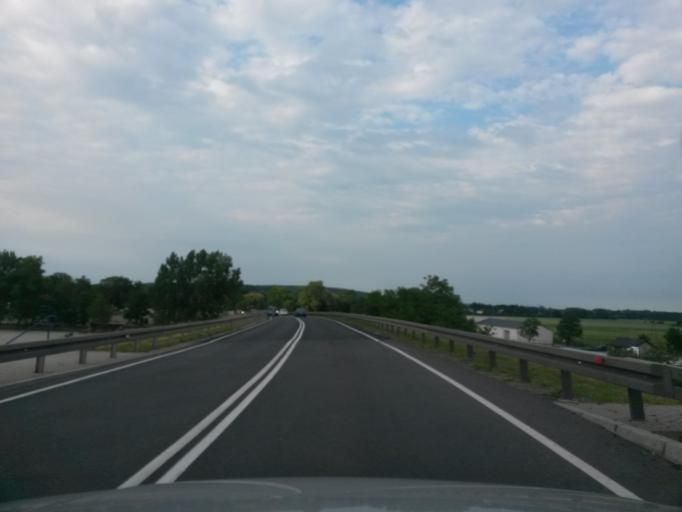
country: PL
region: Lower Silesian Voivodeship
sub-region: Powiat swidnicki
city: Strzegom
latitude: 50.9586
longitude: 16.3627
